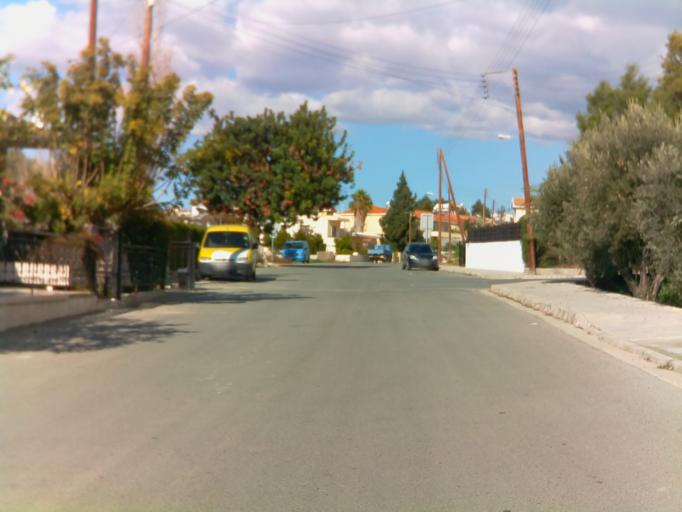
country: CY
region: Limassol
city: Pissouri
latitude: 34.6645
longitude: 32.6976
